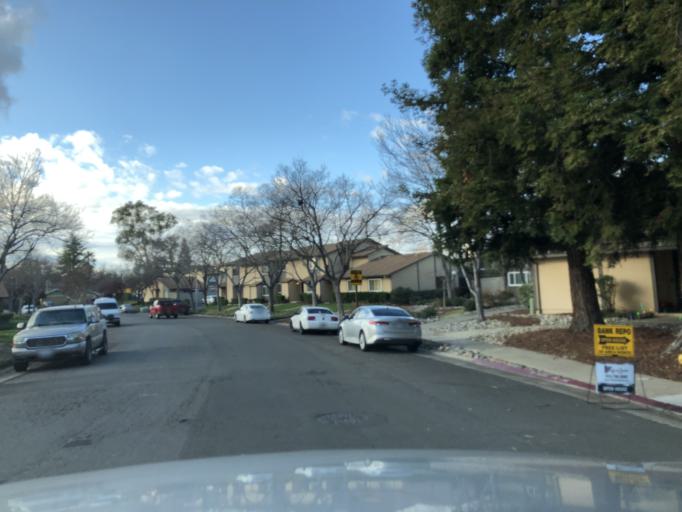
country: US
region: California
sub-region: Sacramento County
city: Foothill Farms
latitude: 38.6569
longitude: -121.3305
